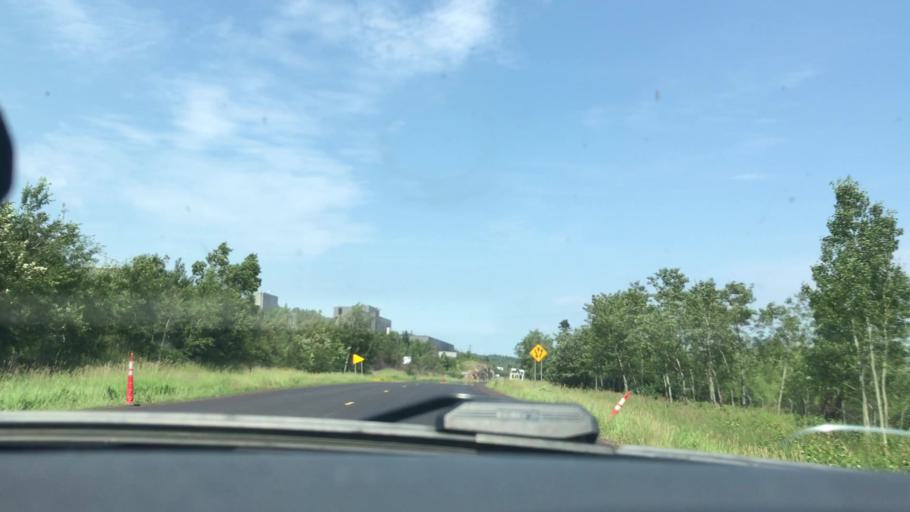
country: US
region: Minnesota
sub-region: Lake County
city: Silver Bay
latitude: 47.2851
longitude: -91.2671
